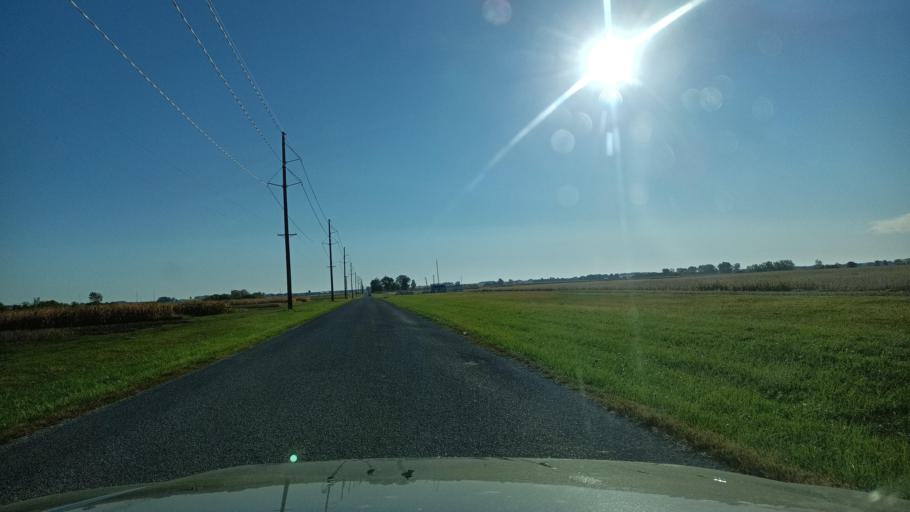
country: US
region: Illinois
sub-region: Champaign County
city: Savoy
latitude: 40.0546
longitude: -88.2373
